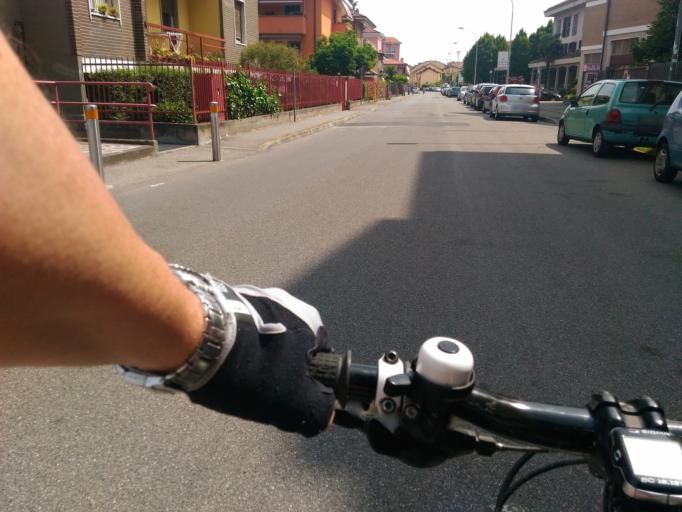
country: IT
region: Lombardy
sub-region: Citta metropolitana di Milano
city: Paullo
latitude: 45.4171
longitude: 9.3935
